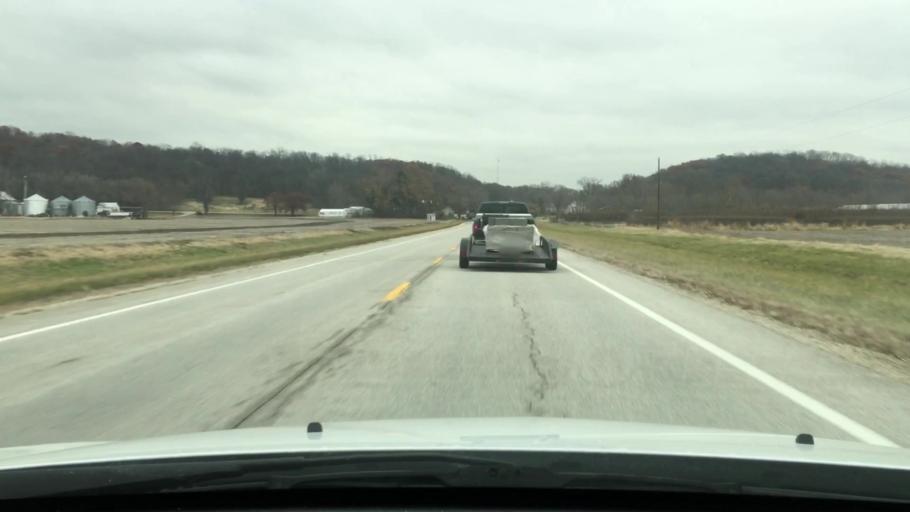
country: US
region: Missouri
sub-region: Pike County
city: Louisiana
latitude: 39.5109
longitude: -90.9745
